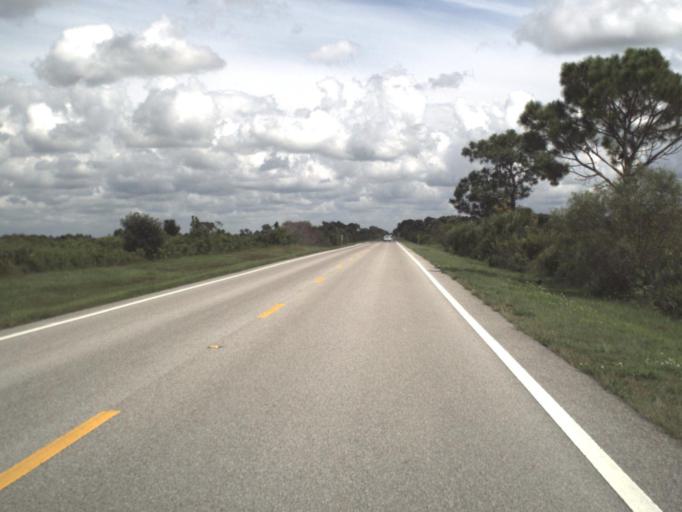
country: US
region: Florida
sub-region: Sarasota County
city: Lake Sarasota
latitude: 27.2217
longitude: -82.2924
